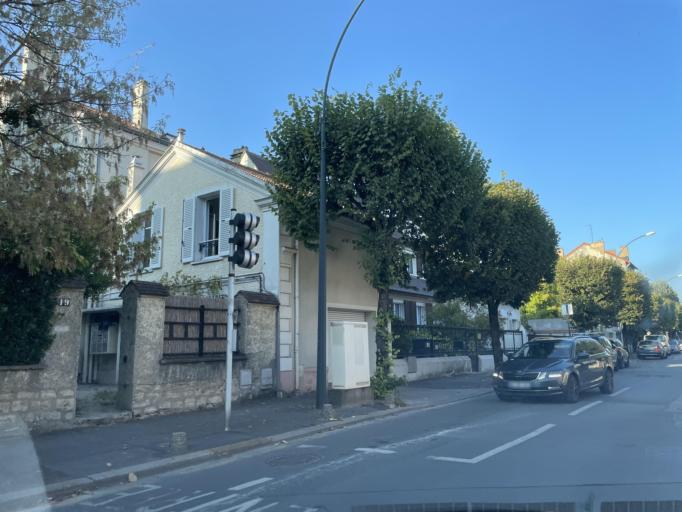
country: FR
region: Ile-de-France
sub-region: Departement du Val-de-Marne
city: Saint-Maur-des-Fosses
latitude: 48.7958
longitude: 2.5151
